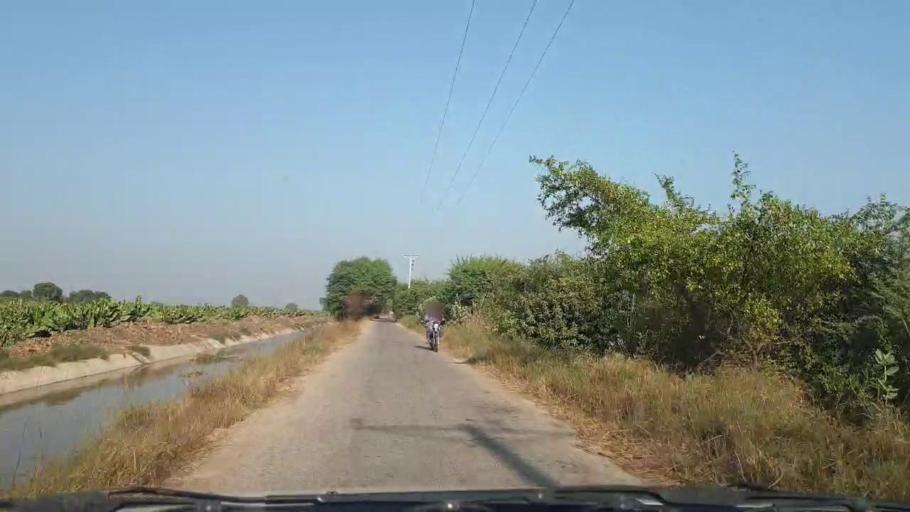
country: PK
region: Sindh
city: Tando Muhammad Khan
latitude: 25.2213
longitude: 68.6325
